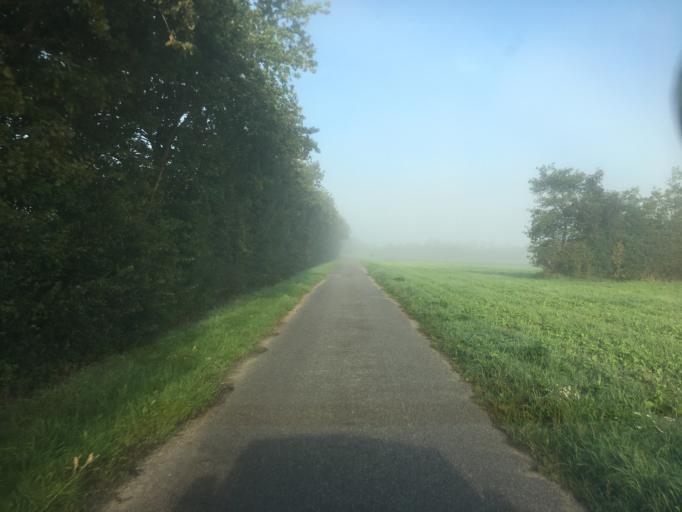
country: DK
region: South Denmark
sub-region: Tonder Kommune
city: Logumkloster
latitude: 55.0177
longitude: 8.9144
